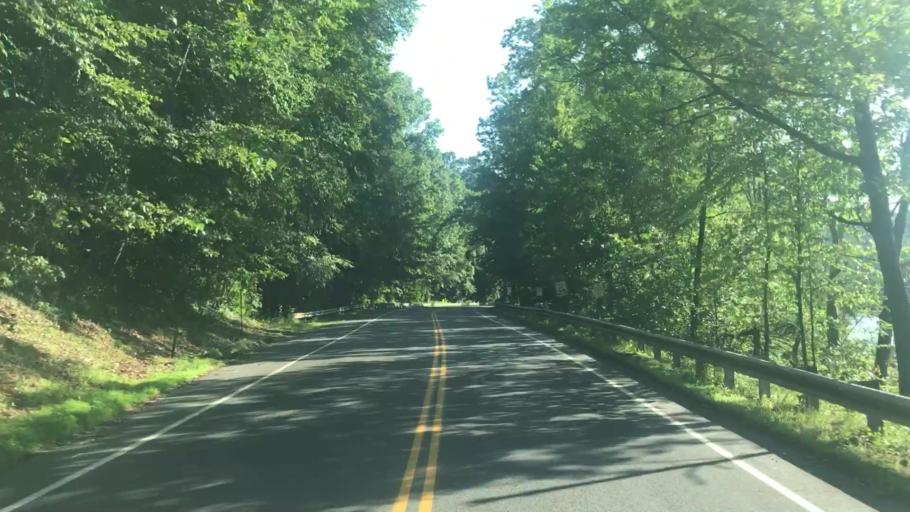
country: US
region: Connecticut
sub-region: New Haven County
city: Heritage Village
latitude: 41.4367
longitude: -73.2540
